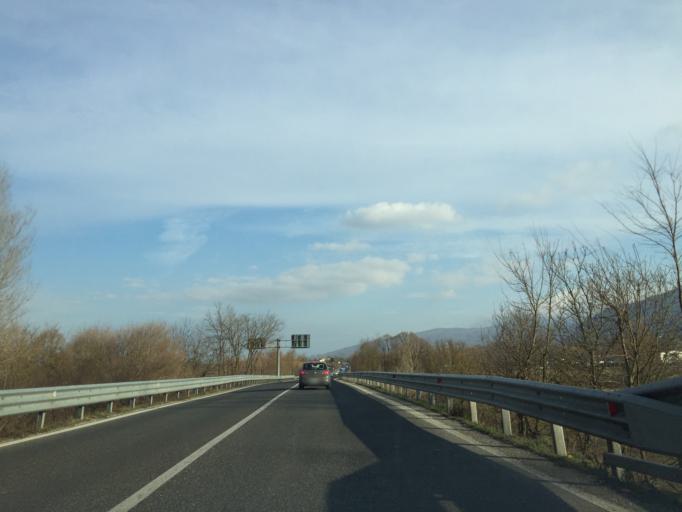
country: IT
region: Molise
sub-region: Provincia di Campobasso
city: Bojano
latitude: 41.4845
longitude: 14.4915
